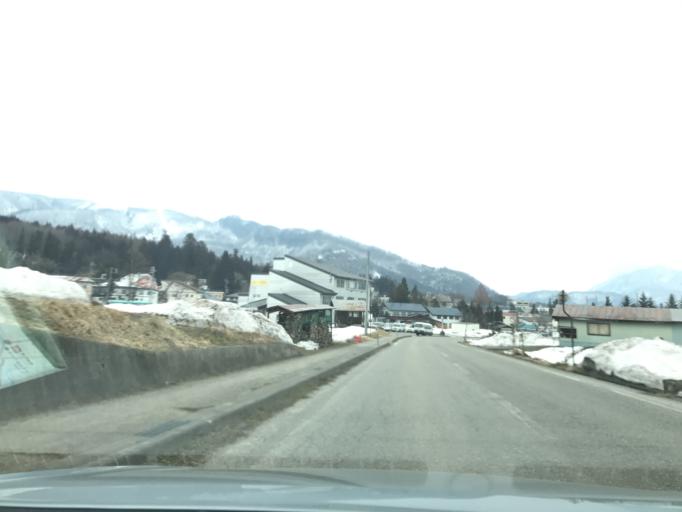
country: JP
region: Nagano
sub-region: Kitaazumi Gun
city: Hakuba
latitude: 36.6979
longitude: 137.8397
